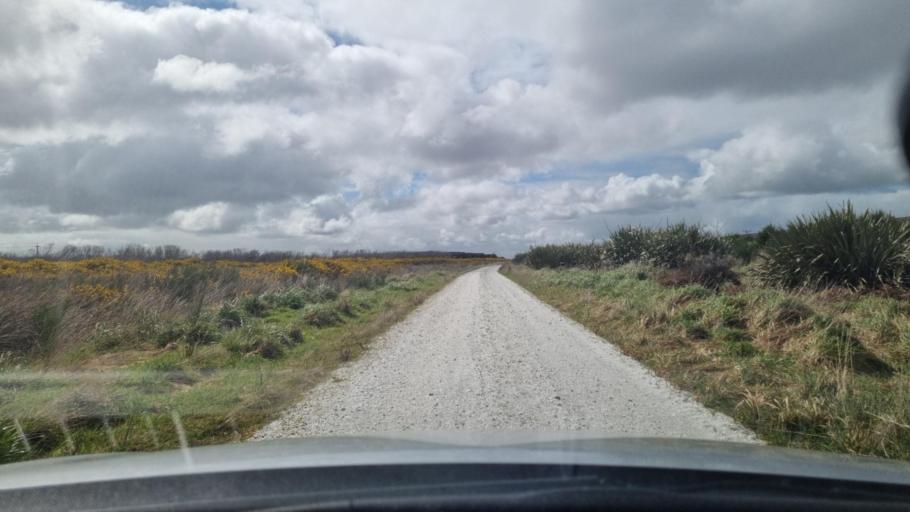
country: NZ
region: Southland
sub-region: Invercargill City
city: Bluff
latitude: -46.5310
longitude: 168.3054
